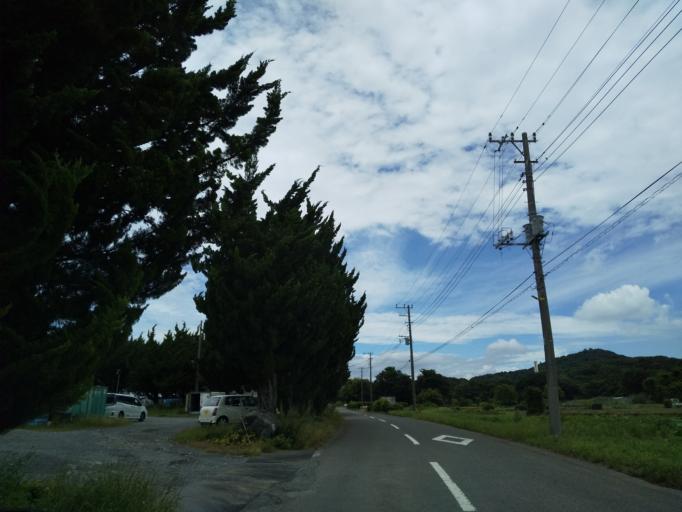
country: JP
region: Kanagawa
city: Zama
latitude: 35.5373
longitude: 139.3010
